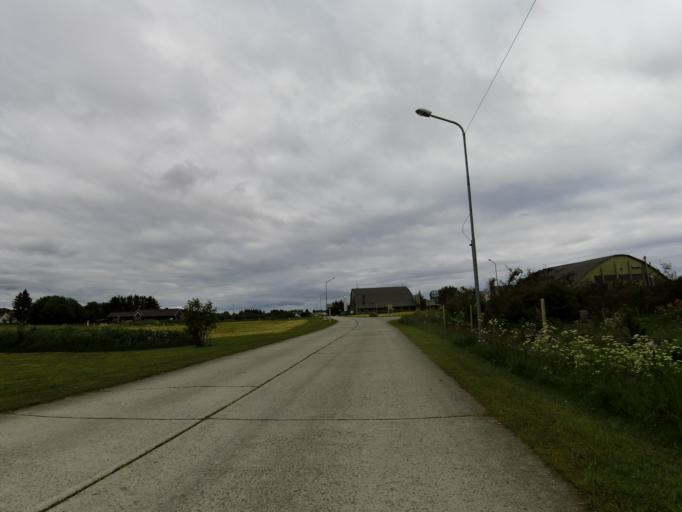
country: NO
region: Vest-Agder
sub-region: Farsund
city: Vestbygd
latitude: 58.1147
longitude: 6.6141
